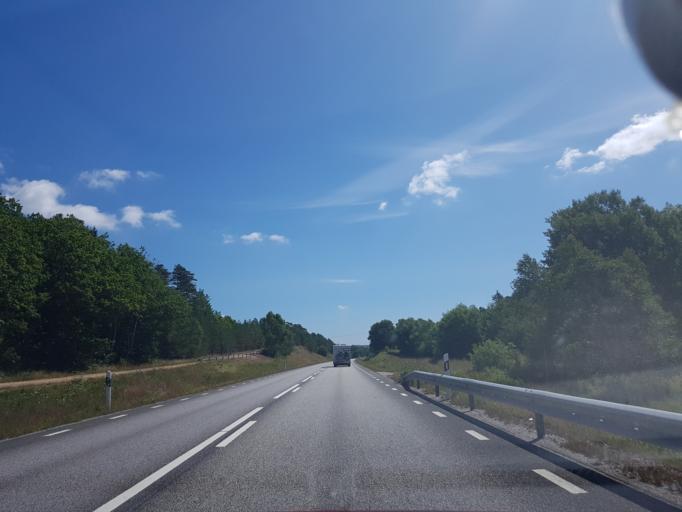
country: SE
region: Vaestra Goetaland
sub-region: Orust
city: Henan
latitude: 58.1552
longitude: 11.5469
